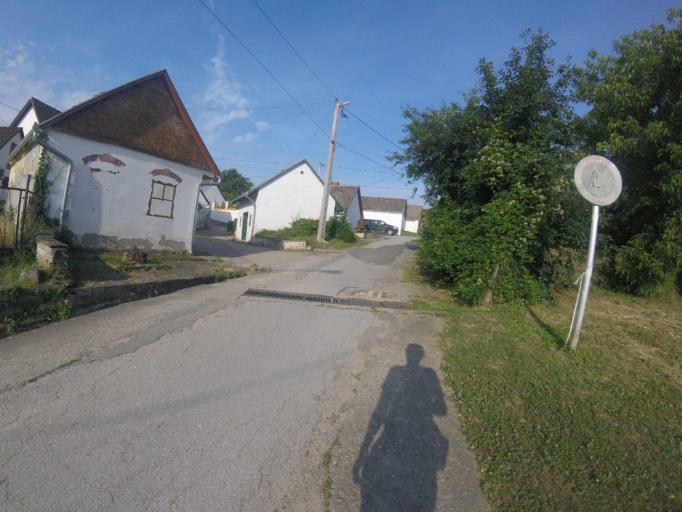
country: HU
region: Baranya
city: Villany
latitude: 45.8685
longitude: 18.4534
